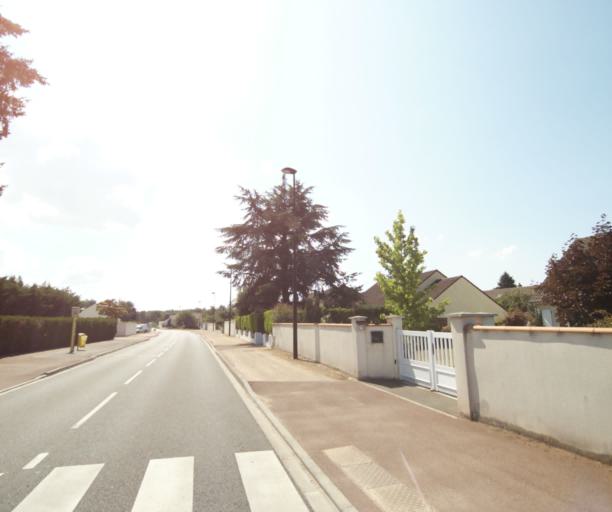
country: FR
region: Centre
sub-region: Departement du Loiret
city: Saint-Cyr-en-Val
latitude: 47.8257
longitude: 1.9755
